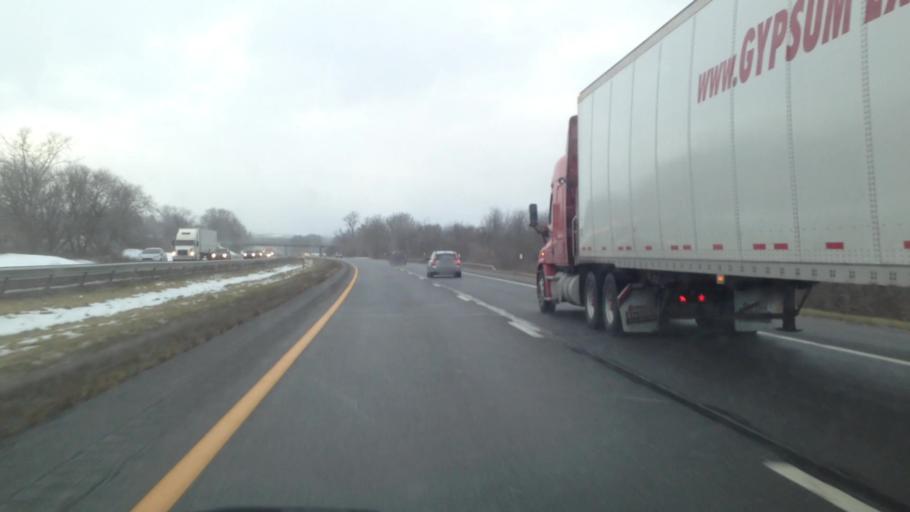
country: US
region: New York
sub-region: Montgomery County
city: Amsterdam
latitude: 42.9096
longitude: -74.1405
